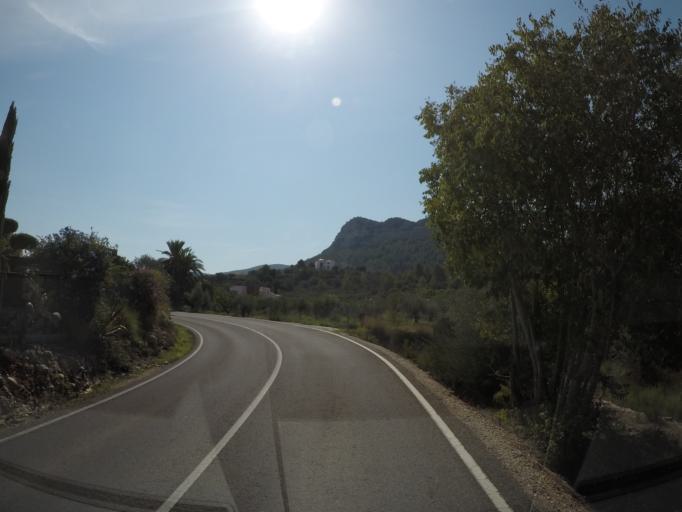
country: ES
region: Valencia
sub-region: Provincia de Alicante
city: Orba
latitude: 38.7803
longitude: -0.0726
